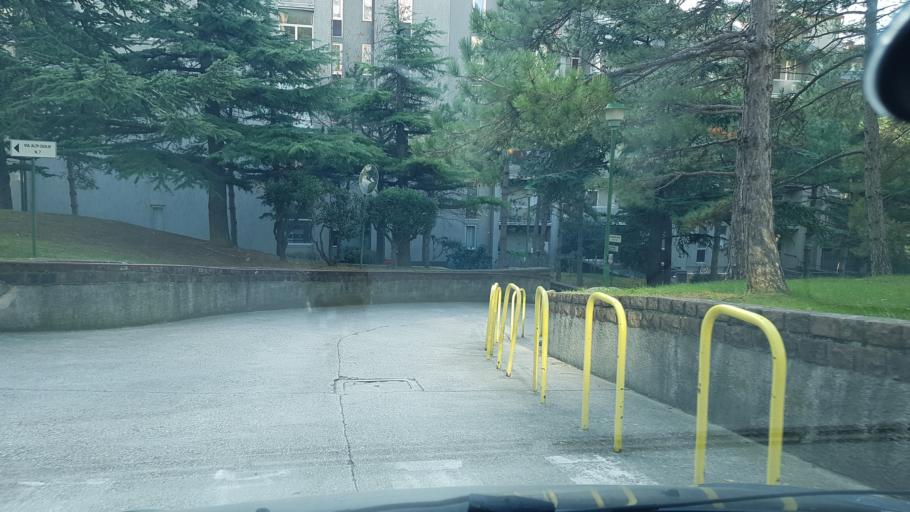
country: IT
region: Friuli Venezia Giulia
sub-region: Provincia di Trieste
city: Domio
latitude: 45.6265
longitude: 13.8198
